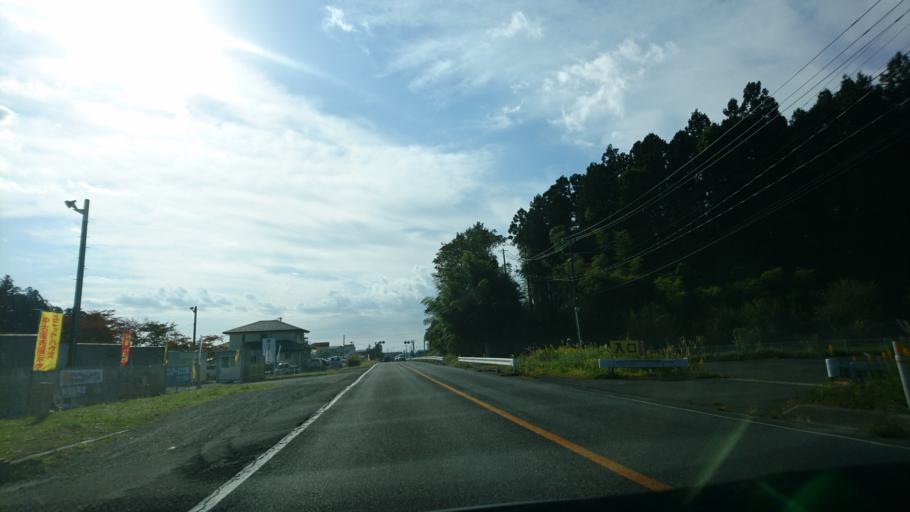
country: JP
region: Miyagi
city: Furukawa
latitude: 38.6242
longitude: 140.9830
